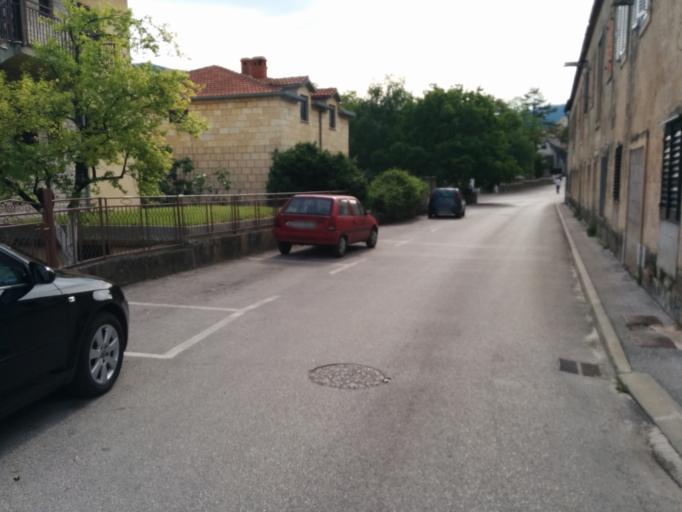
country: HR
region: Splitsko-Dalmatinska
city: Sinj
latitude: 43.7005
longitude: 16.6394
